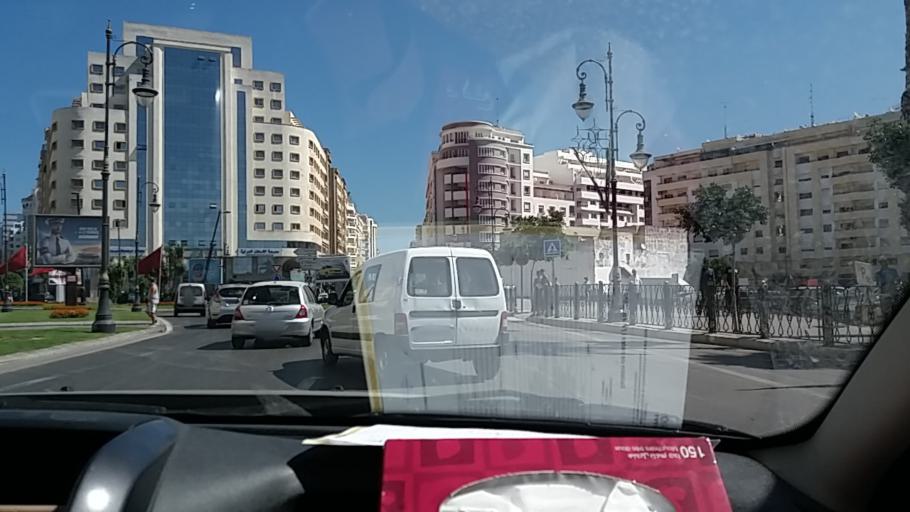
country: MA
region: Tanger-Tetouan
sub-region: Tanger-Assilah
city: Tangier
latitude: 35.7722
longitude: -5.8022
